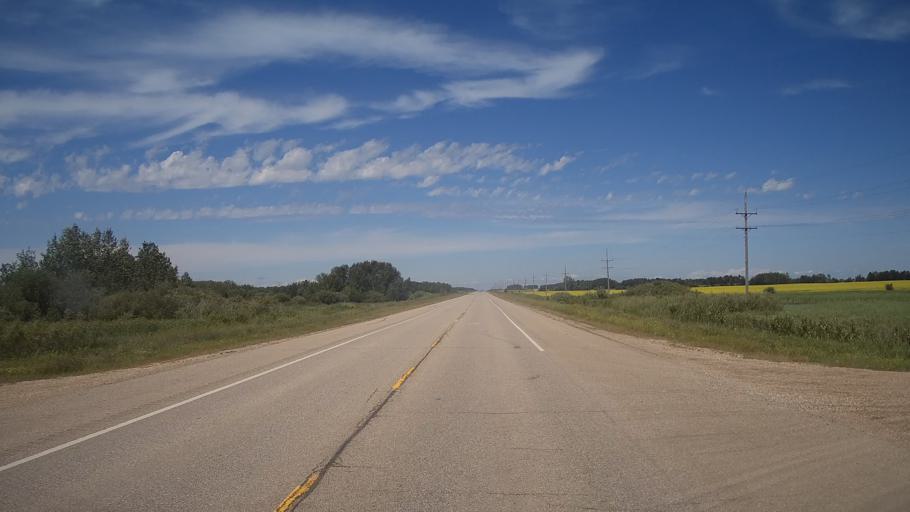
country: CA
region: Saskatchewan
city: Langenburg
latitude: 50.6531
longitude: -101.2760
